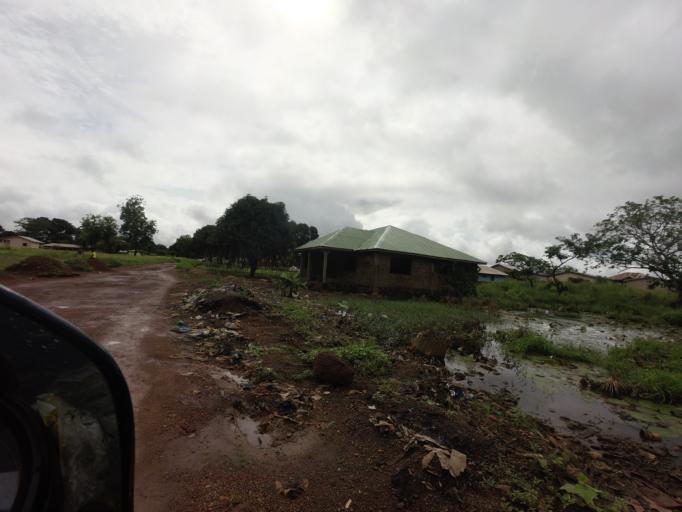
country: SL
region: Northern Province
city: Kambia
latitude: 9.1085
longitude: -12.9307
